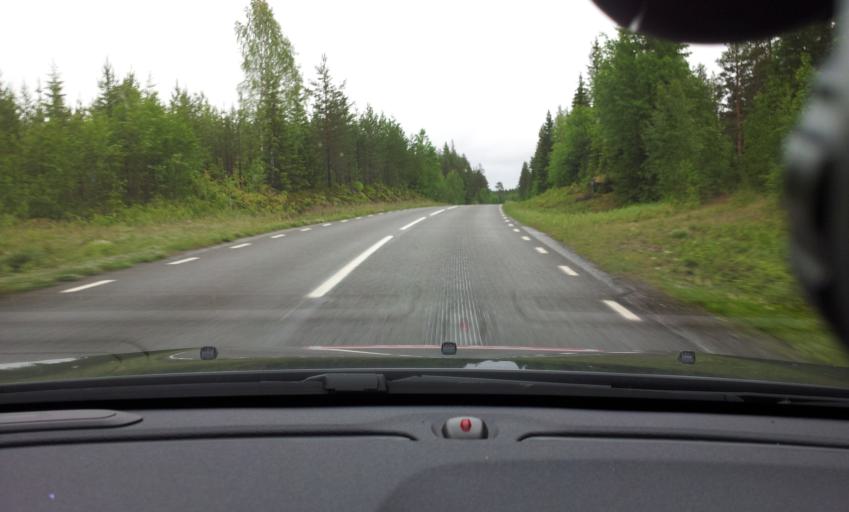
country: SE
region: Jaemtland
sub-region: Stroemsunds Kommun
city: Stroemsund
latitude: 63.4226
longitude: 15.5362
